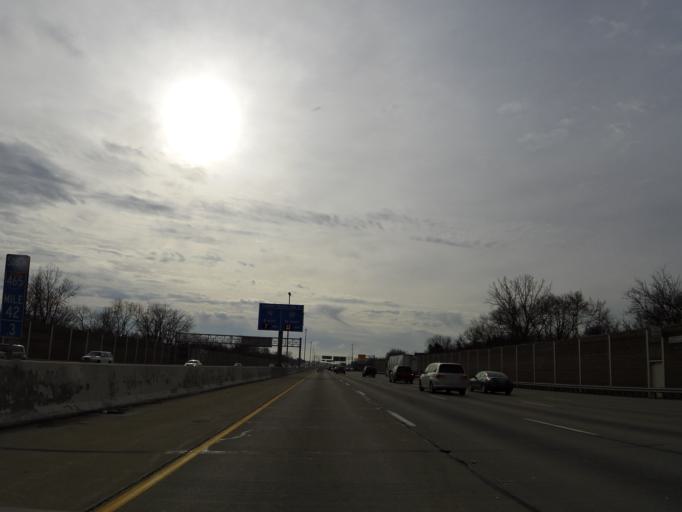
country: US
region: Indiana
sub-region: Marion County
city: Lawrence
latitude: 39.8202
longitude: -86.0311
